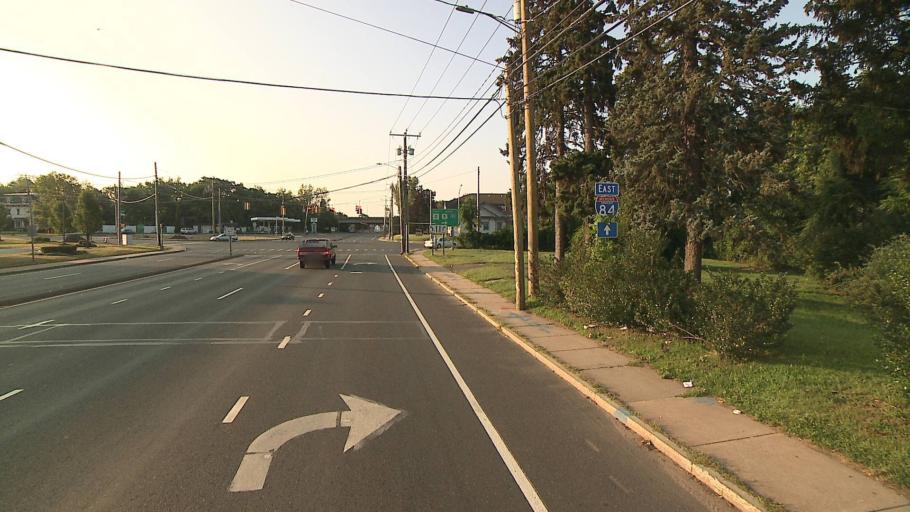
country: US
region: Connecticut
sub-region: Hartford County
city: East Hartford
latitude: 41.7609
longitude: -72.6452
